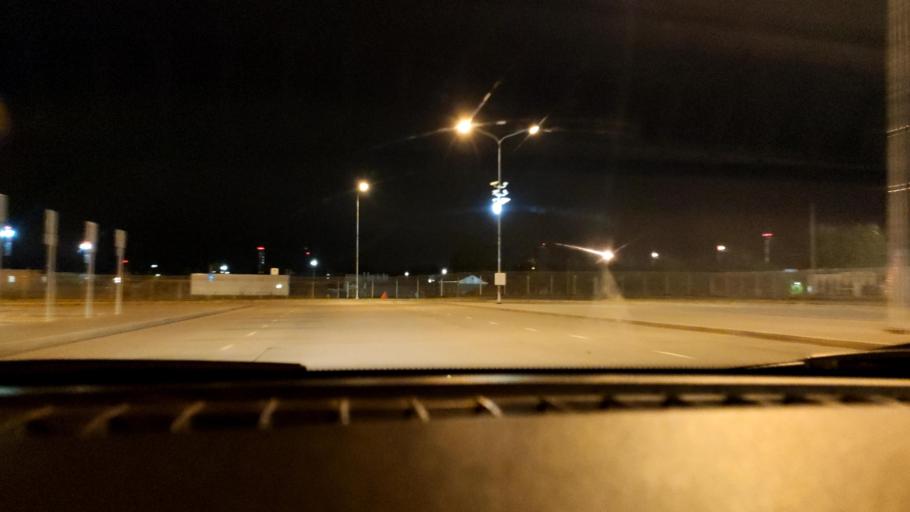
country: RU
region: Perm
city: Kultayevo
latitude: 57.9169
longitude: 56.0097
